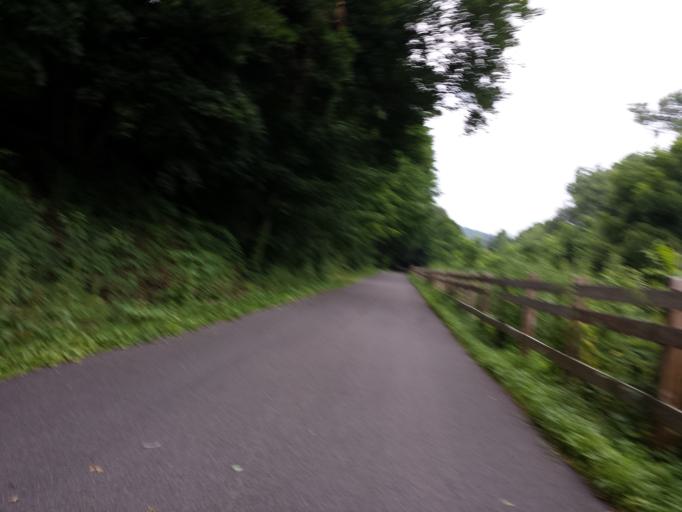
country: US
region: New York
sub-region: Ulster County
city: Highland
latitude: 41.7132
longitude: -73.9651
